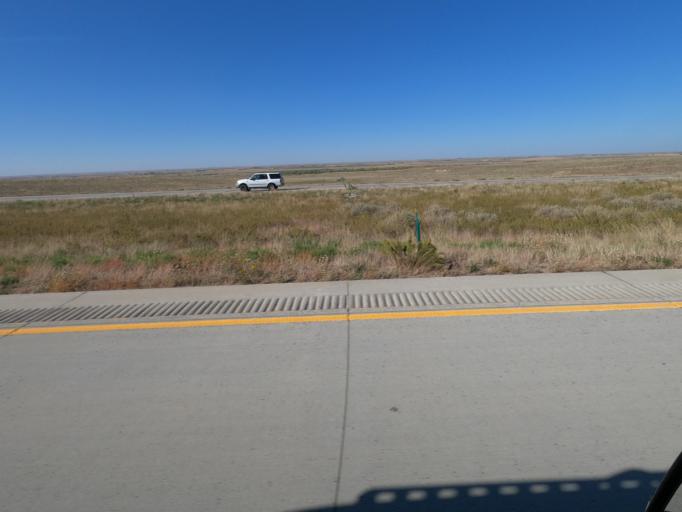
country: US
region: Nebraska
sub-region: Deuel County
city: Chappell
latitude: 40.9184
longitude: -102.4666
